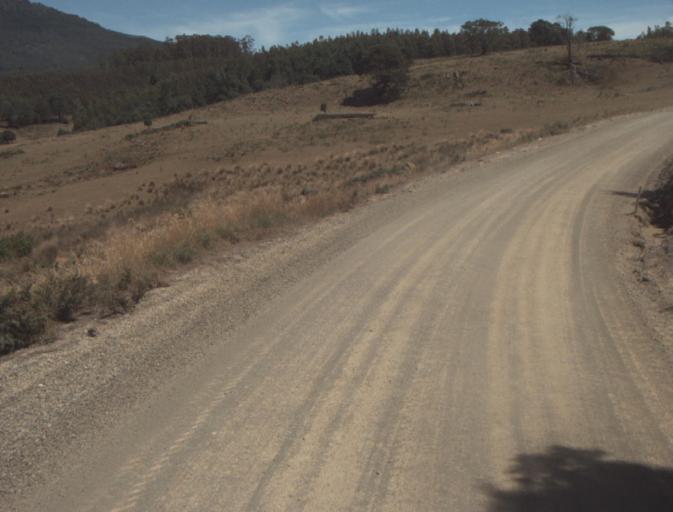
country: AU
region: Tasmania
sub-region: Dorset
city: Scottsdale
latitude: -41.3296
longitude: 147.4422
